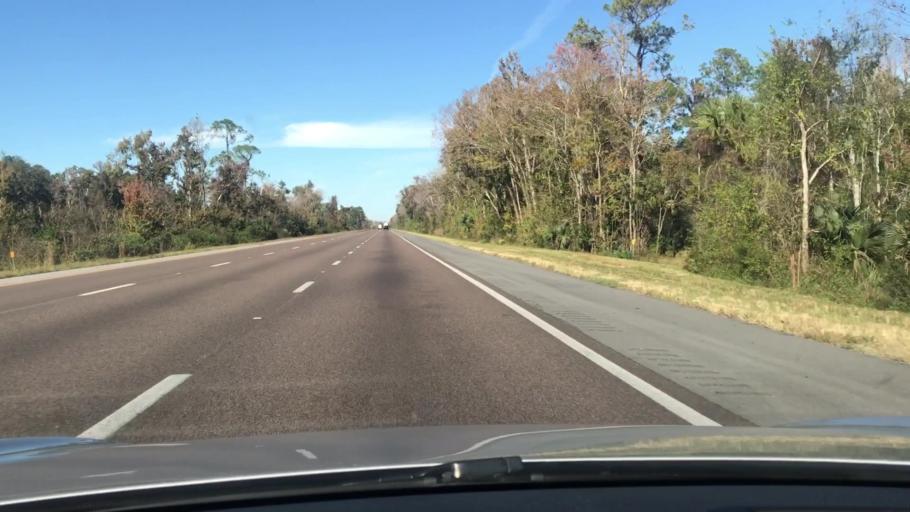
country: US
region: Florida
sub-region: Volusia County
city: Oak Hill
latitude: 28.8843
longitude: -80.9245
